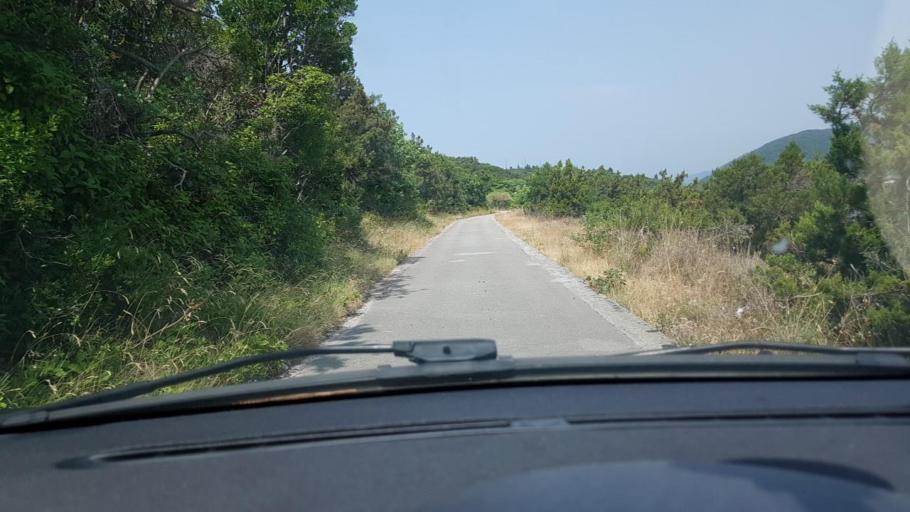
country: ME
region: Herceg Novi
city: Herceg-Novi
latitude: 42.3964
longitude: 18.5262
